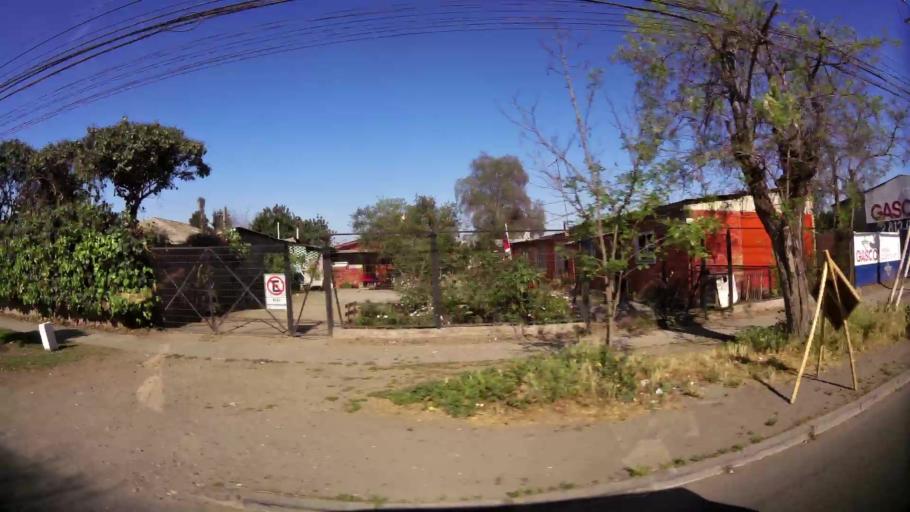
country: CL
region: Santiago Metropolitan
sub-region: Provincia de Talagante
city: Penaflor
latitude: -33.6053
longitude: -70.8777
